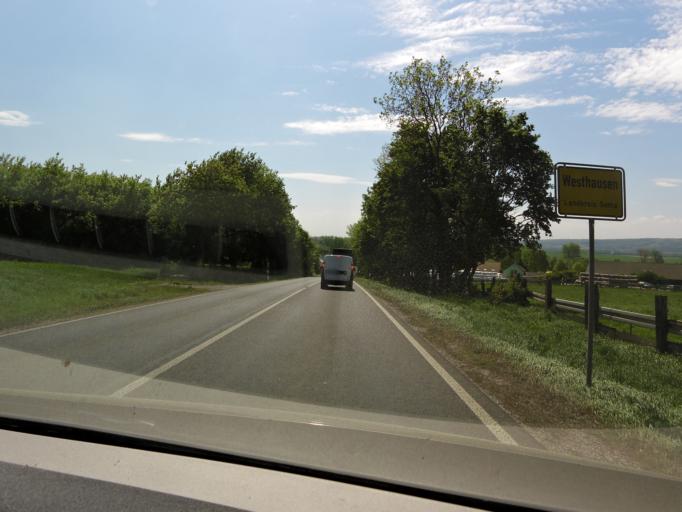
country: DE
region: Thuringia
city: Westhausen
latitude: 51.0182
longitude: 10.6827
